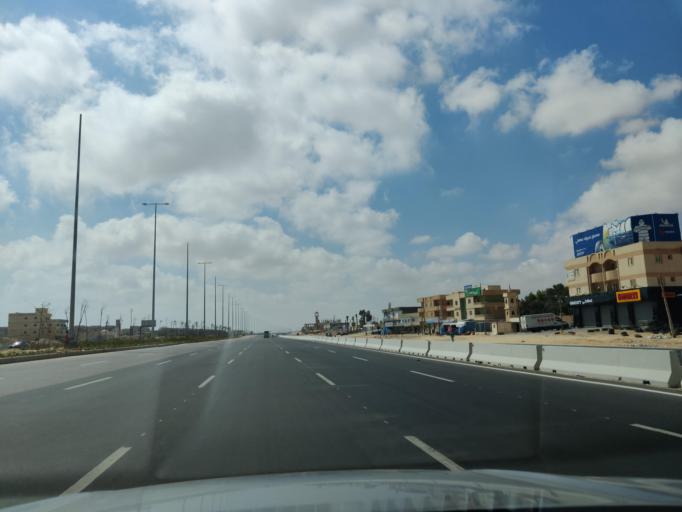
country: EG
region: Muhafazat Matruh
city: Al `Alamayn
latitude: 30.9441
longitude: 28.7790
